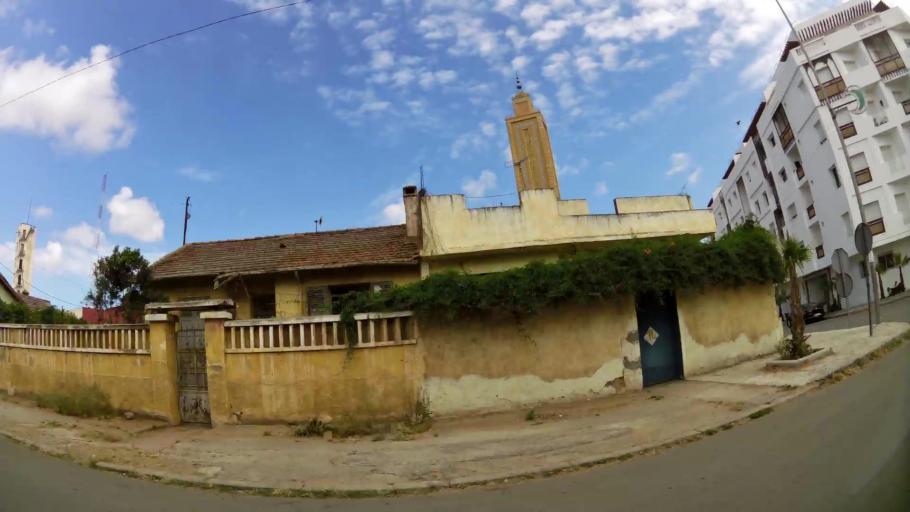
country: MA
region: Gharb-Chrarda-Beni Hssen
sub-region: Kenitra Province
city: Kenitra
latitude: 34.2537
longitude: -6.5840
